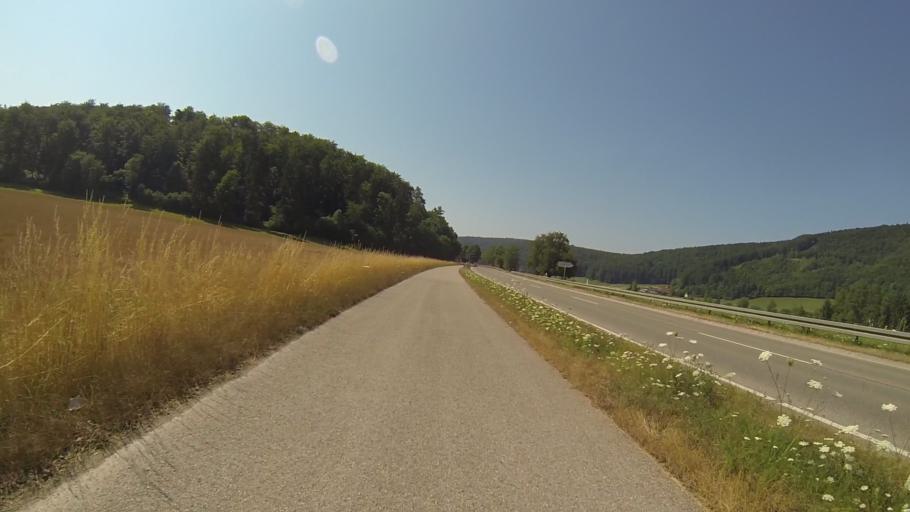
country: DE
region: Baden-Wuerttemberg
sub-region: Regierungsbezirk Stuttgart
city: Konigsbronn
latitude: 48.7585
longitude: 10.1036
